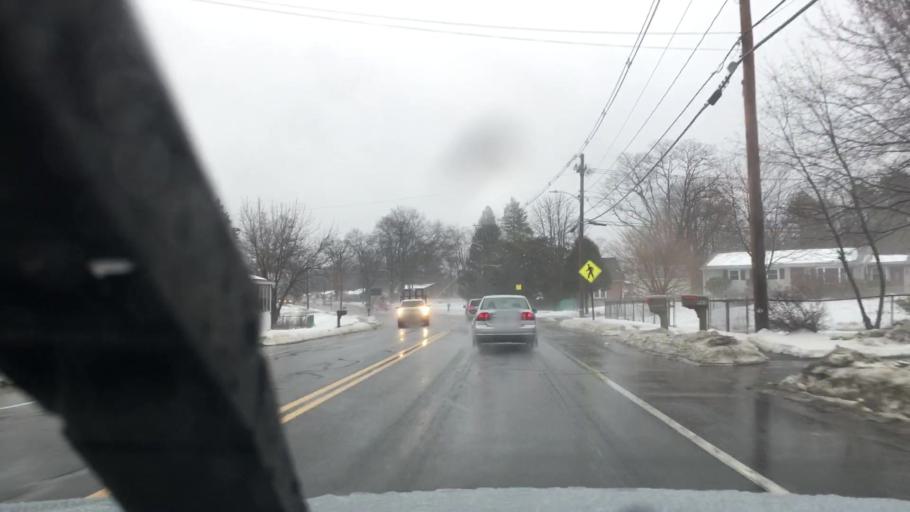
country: US
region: Massachusetts
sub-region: Hampden County
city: Ludlow
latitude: 42.1758
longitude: -72.5276
